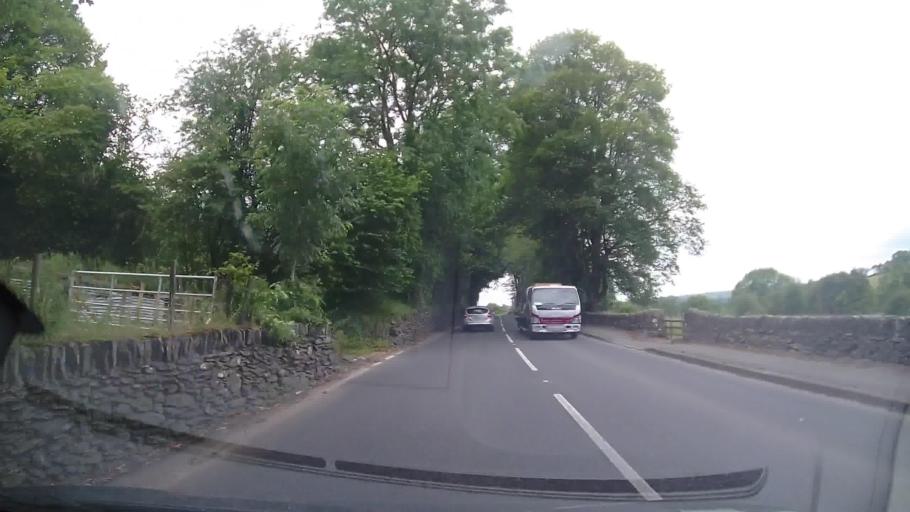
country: GB
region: Wales
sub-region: Denbighshire
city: Corwen
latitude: 52.9809
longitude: -3.3568
